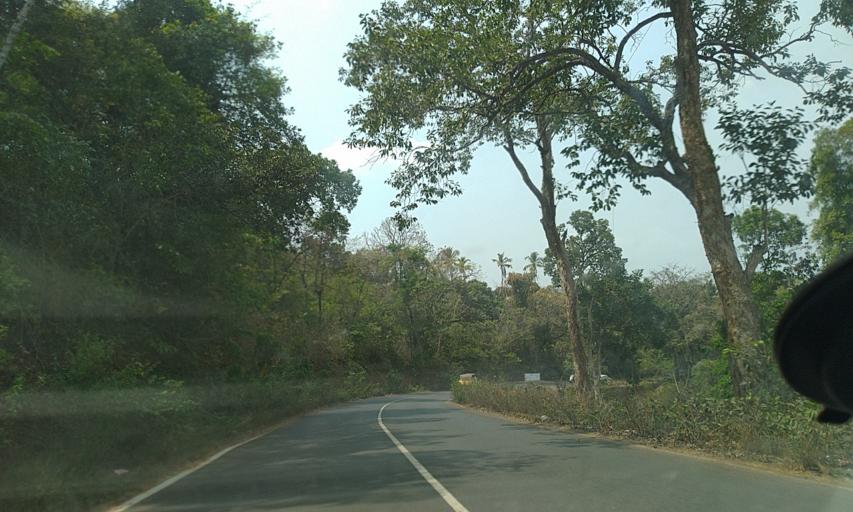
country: IN
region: Goa
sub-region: North Goa
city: Pernem
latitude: 15.7107
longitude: 73.7985
